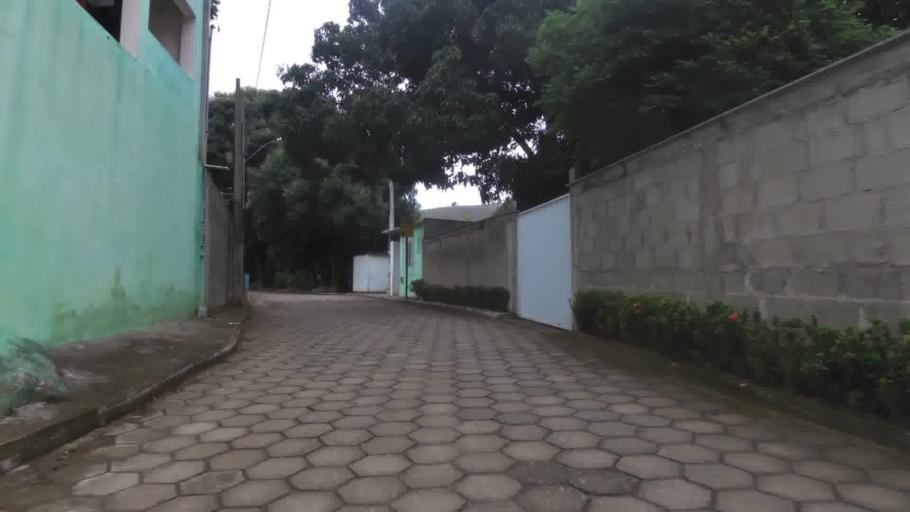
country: BR
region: Espirito Santo
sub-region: Iconha
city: Iconha
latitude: -20.7751
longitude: -40.8281
